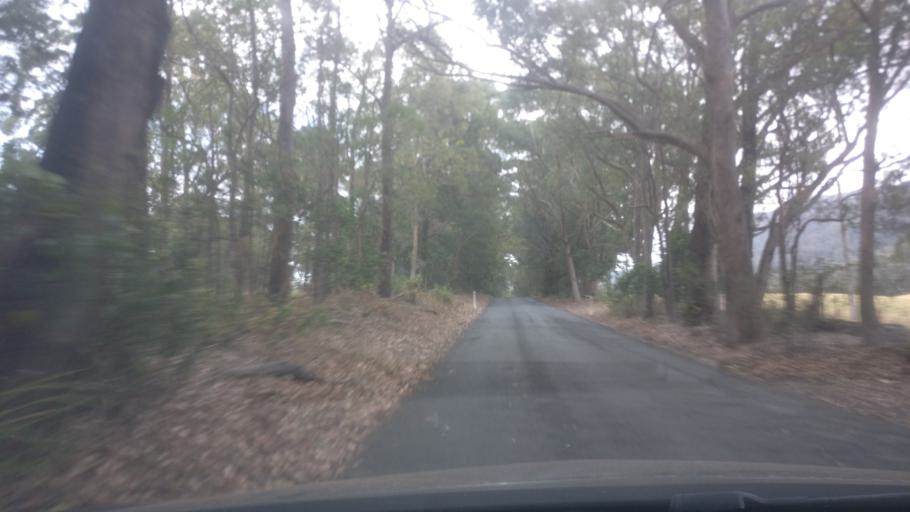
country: AU
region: New South Wales
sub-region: Shoalhaven Shire
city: Kangaroo Valley
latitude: -34.7210
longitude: 150.4681
